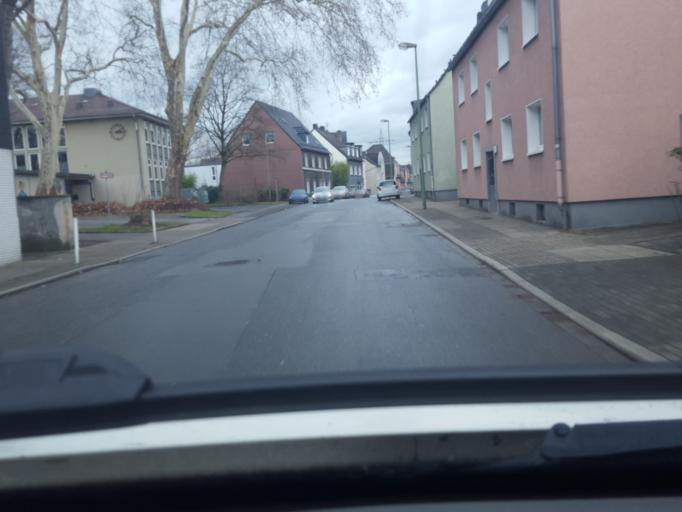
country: DE
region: North Rhine-Westphalia
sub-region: Regierungsbezirk Dusseldorf
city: Essen
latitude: 51.4663
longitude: 6.9565
